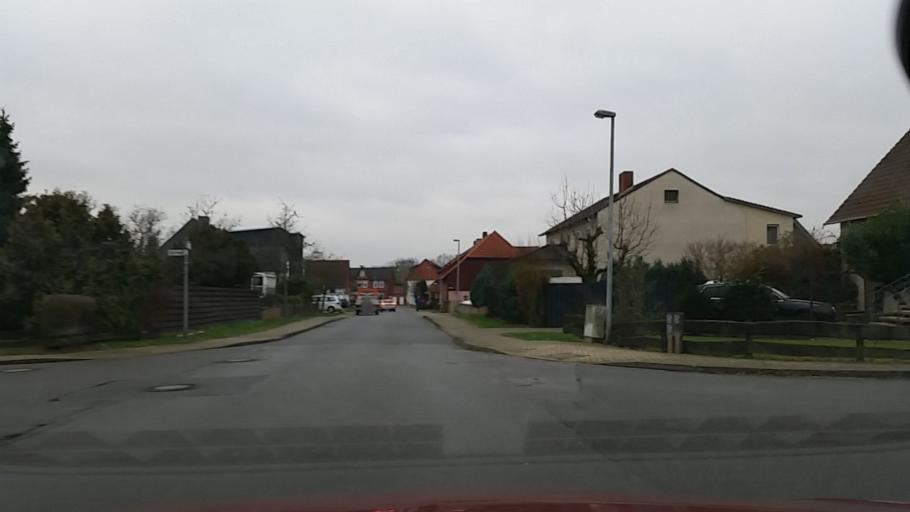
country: DE
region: Lower Saxony
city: Wolfsburg
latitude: 52.4454
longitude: 10.7775
